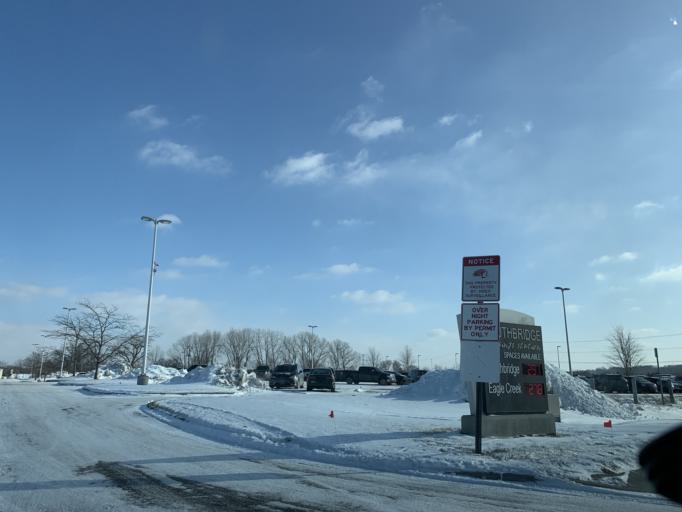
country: US
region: Minnesota
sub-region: Scott County
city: Prior Lake
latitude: 44.7799
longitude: -93.4096
